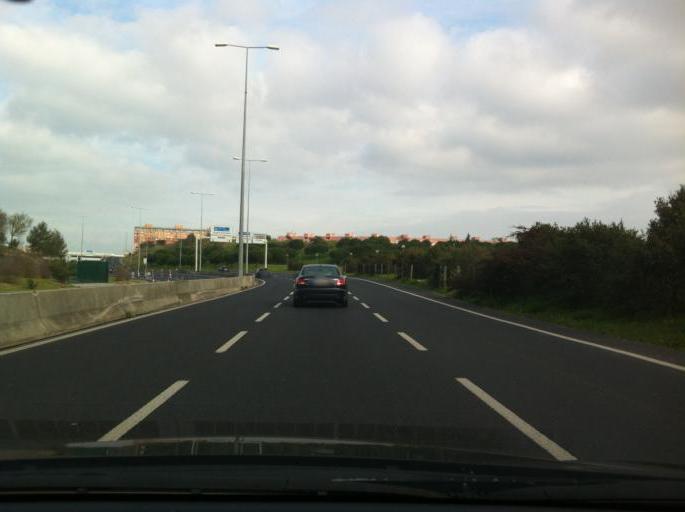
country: PT
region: Lisbon
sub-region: Lisbon
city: Lisbon
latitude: 38.7468
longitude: -9.1260
